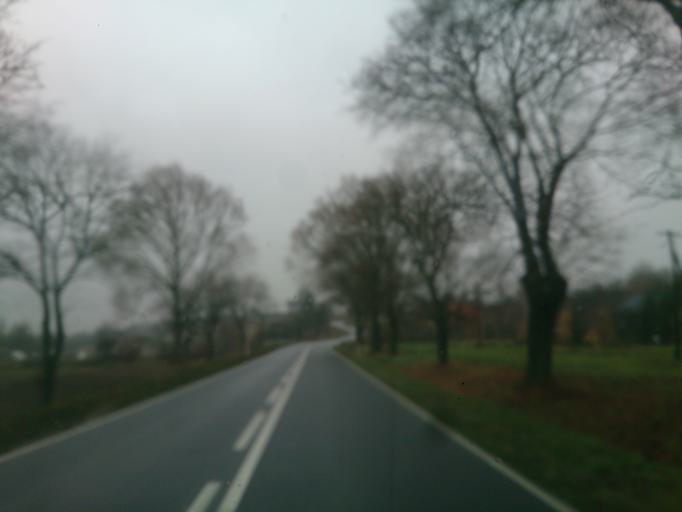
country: PL
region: Kujawsko-Pomorskie
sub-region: Powiat rypinski
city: Rypin
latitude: 53.1415
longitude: 19.3813
